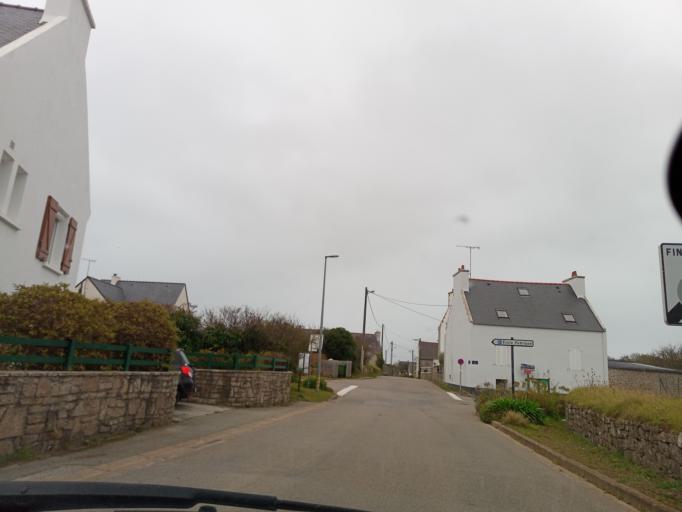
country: FR
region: Brittany
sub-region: Departement du Finistere
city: Esquibien
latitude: 48.0222
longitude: -4.5635
